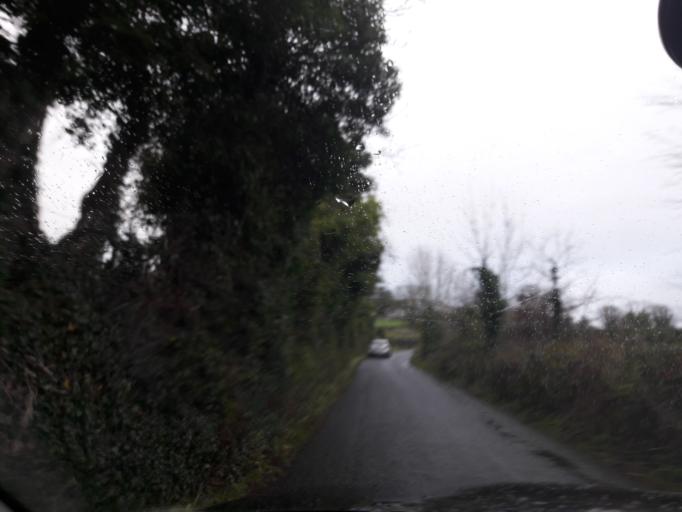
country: IE
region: Ulster
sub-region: County Donegal
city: Ramelton
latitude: 55.2097
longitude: -7.6203
